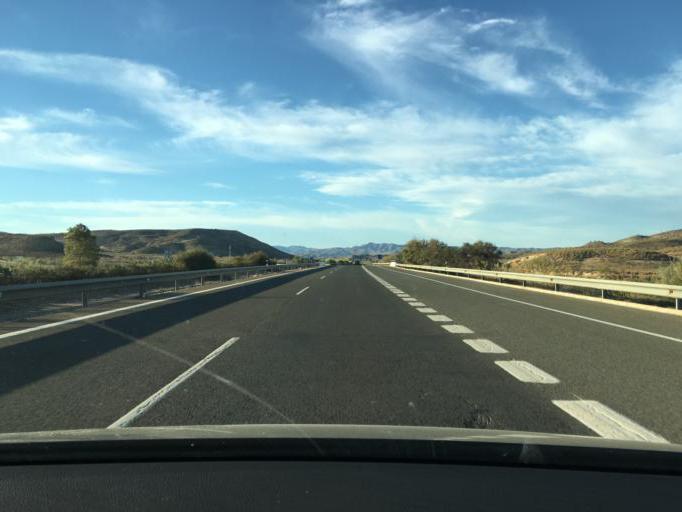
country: ES
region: Andalusia
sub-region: Provincia de Almeria
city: Sorbas
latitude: 37.0657
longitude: -2.0542
